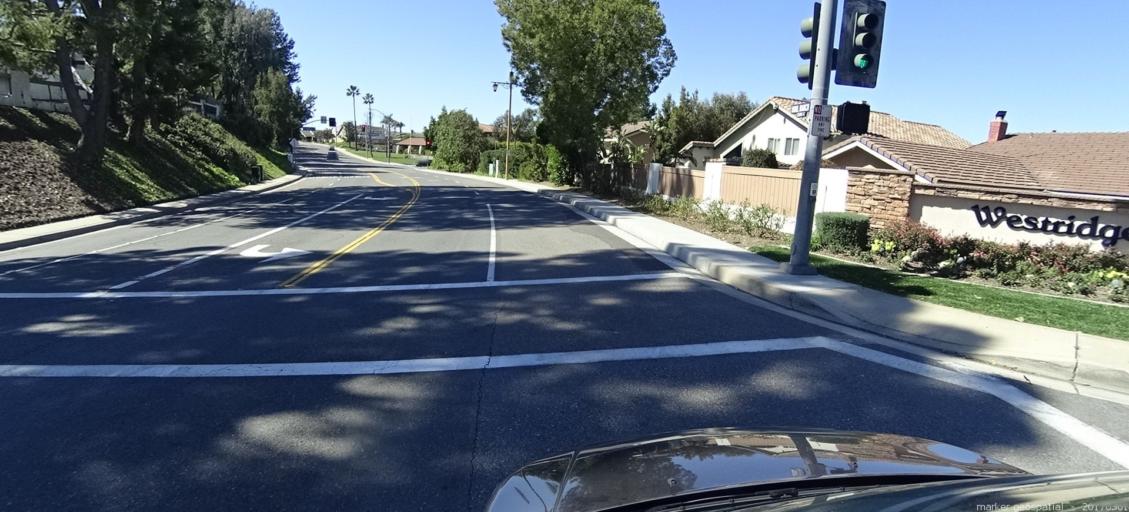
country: US
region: California
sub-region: Orange County
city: Villa Park
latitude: 33.8445
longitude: -117.7998
